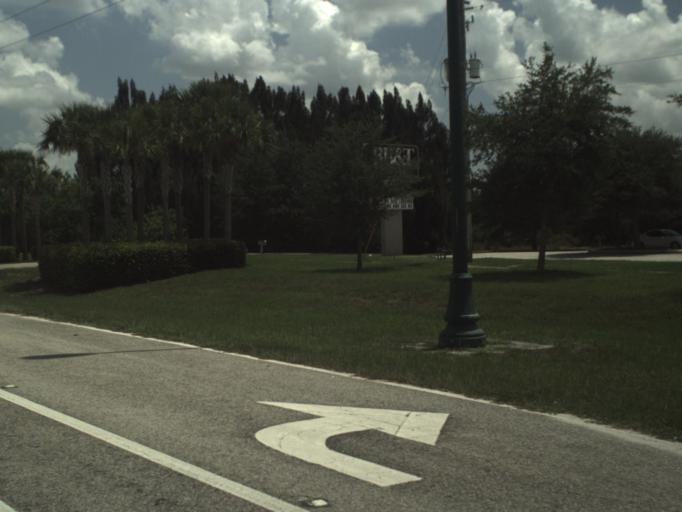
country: US
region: Florida
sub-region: Martin County
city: Hobe Sound
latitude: 27.0653
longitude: -80.1393
